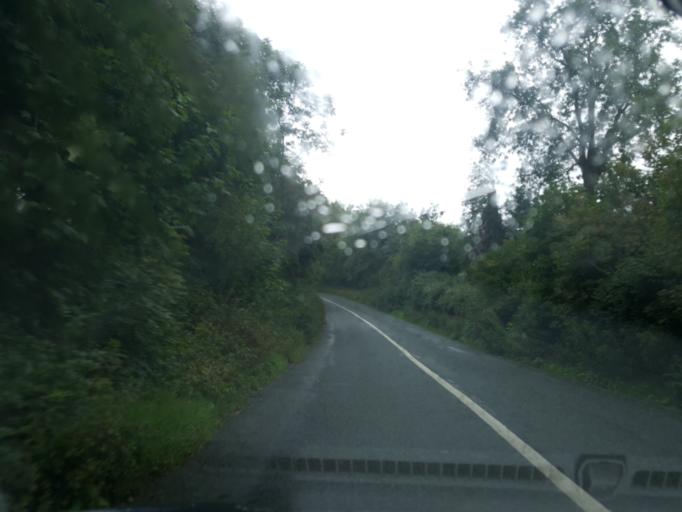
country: IE
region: Leinster
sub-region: Wicklow
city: Valleymount
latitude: 53.1283
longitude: -6.5864
